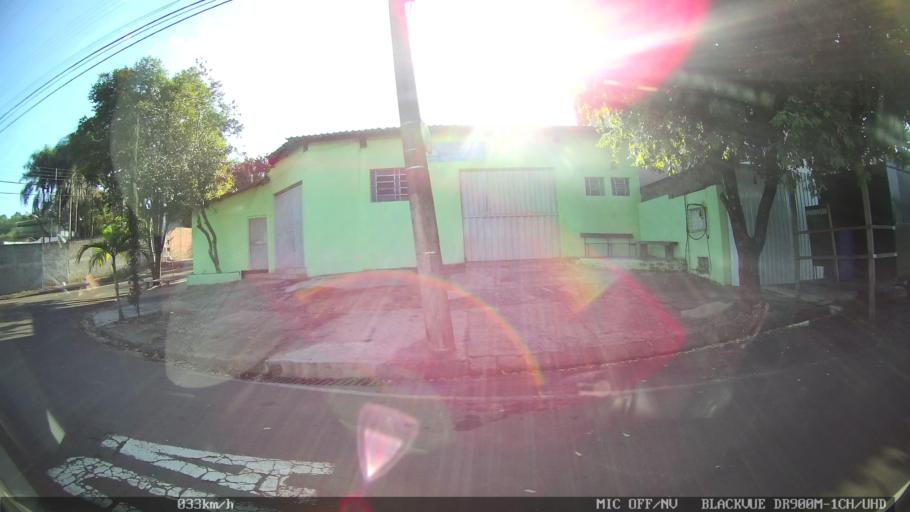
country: BR
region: Sao Paulo
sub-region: Piracicaba
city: Piracicaba
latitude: -22.6890
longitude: -47.6340
